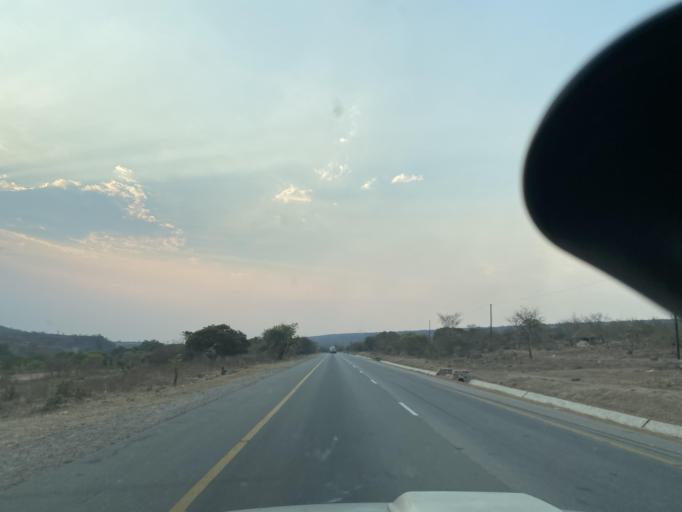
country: ZM
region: Lusaka
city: Kafue
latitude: -15.9019
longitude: 28.3468
